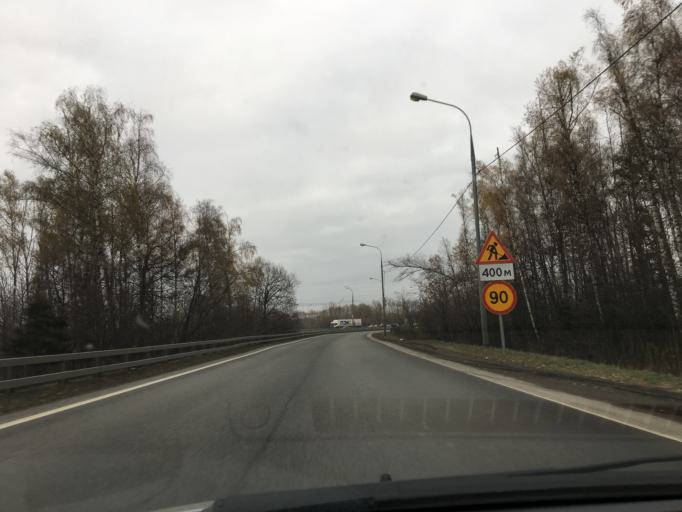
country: RU
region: Moscow
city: Biryulevo
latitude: 55.5741
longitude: 37.6872
